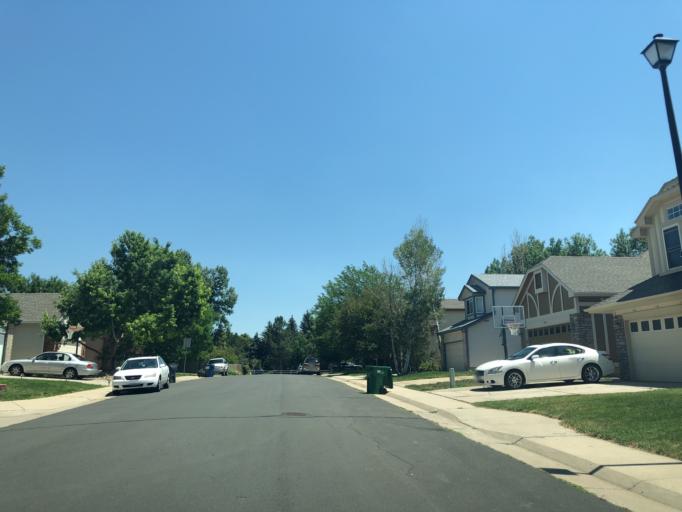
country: US
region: Colorado
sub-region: Arapahoe County
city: Dove Valley
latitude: 39.6263
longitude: -104.7734
